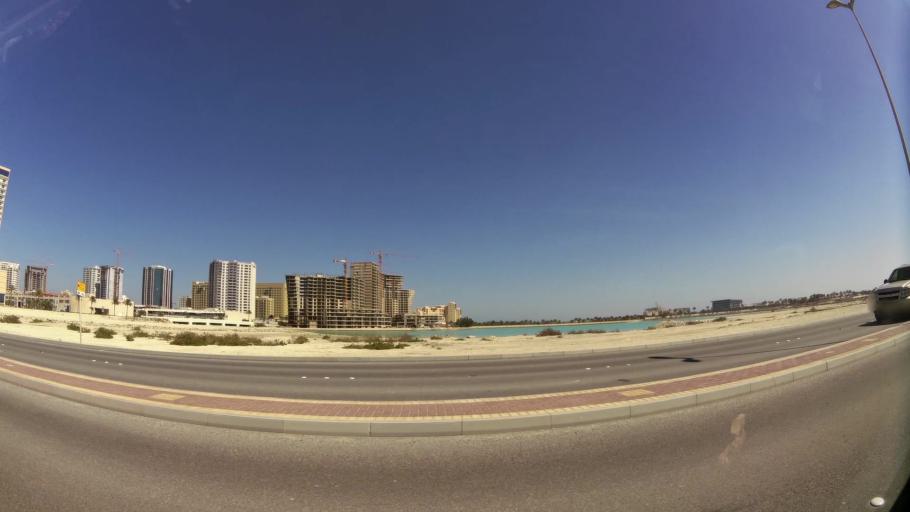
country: BH
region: Muharraq
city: Al Hadd
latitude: 26.2852
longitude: 50.6592
